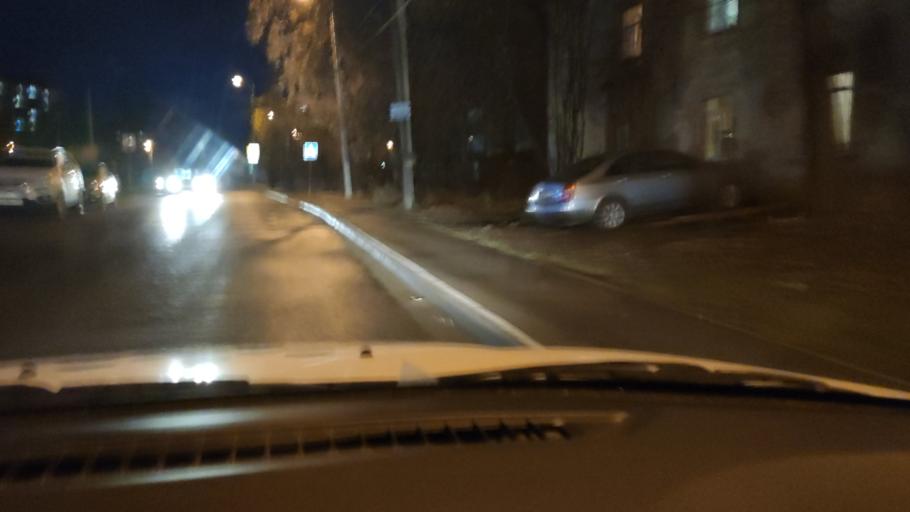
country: RU
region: Perm
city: Perm
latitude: 57.9885
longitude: 56.2234
